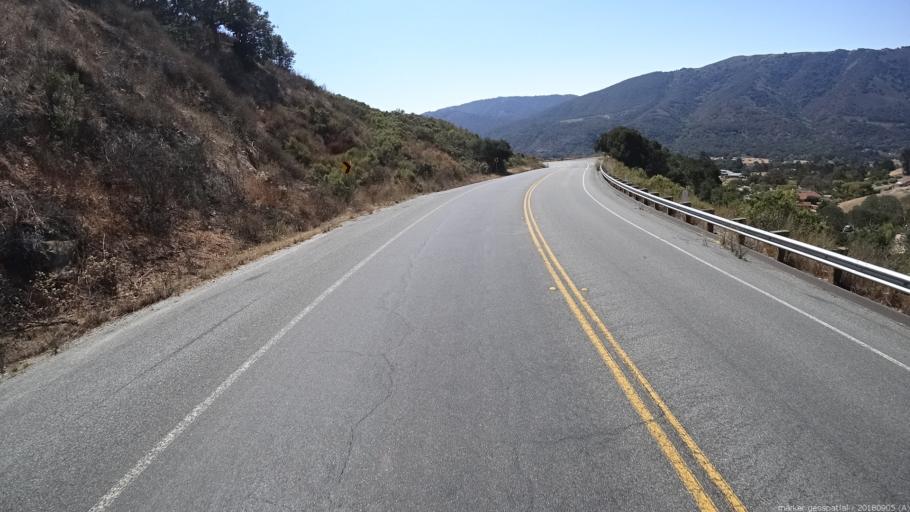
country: US
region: California
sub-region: Monterey County
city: Carmel Valley Village
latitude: 36.5147
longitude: -121.7560
